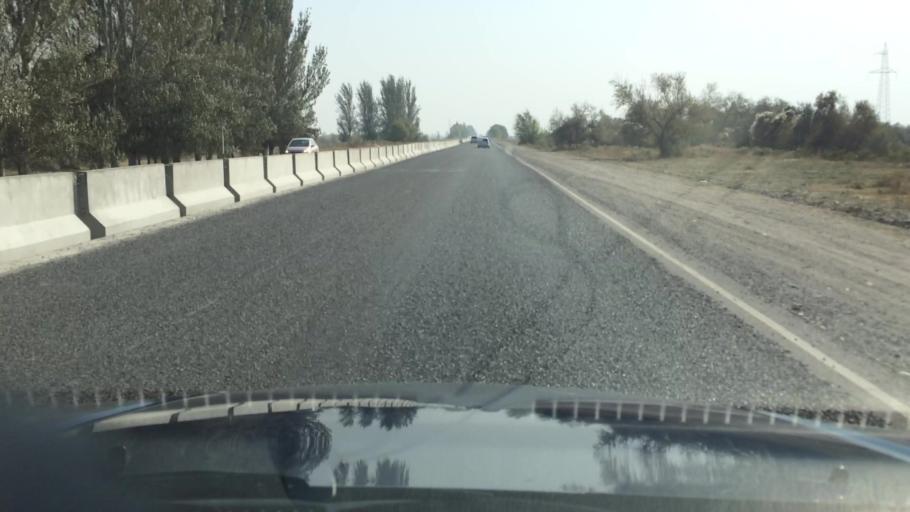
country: KG
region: Chuy
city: Kant
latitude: 42.9732
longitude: 74.8976
